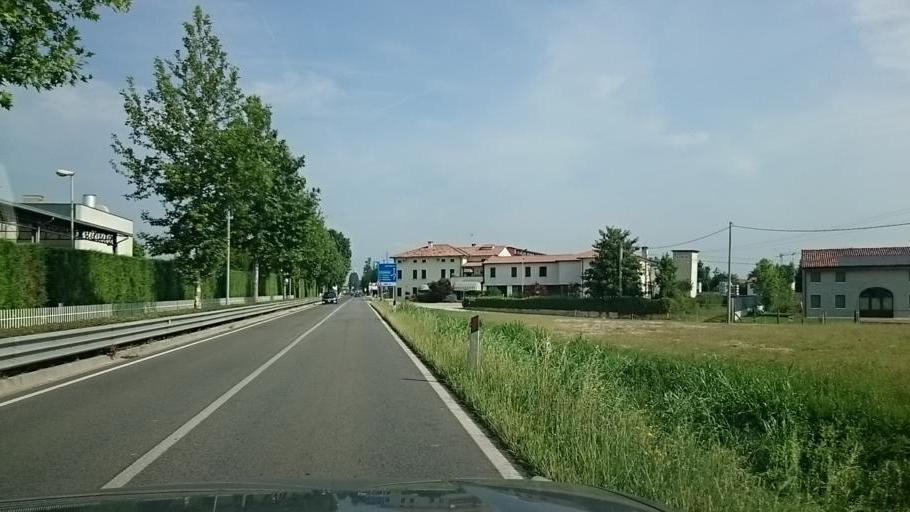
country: IT
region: Veneto
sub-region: Provincia di Treviso
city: Castelfranco Veneto
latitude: 45.6537
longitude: 11.9419
